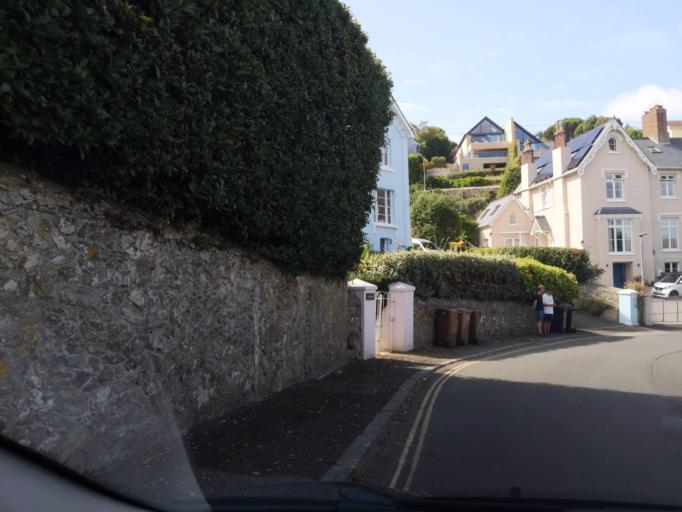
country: GB
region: England
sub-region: Devon
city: Salcombe
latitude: 50.2371
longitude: -3.7692
